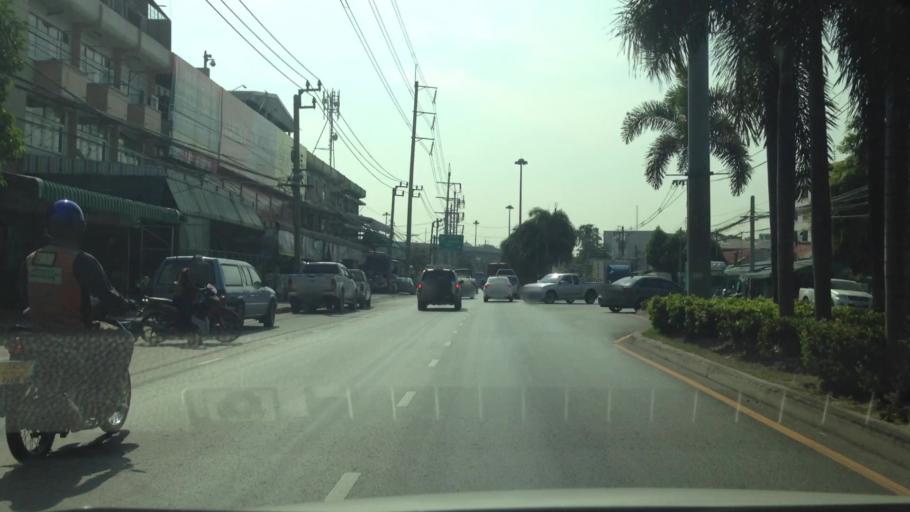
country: TH
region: Samut Prakan
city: Samut Prakan
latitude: 13.5782
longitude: 100.6031
